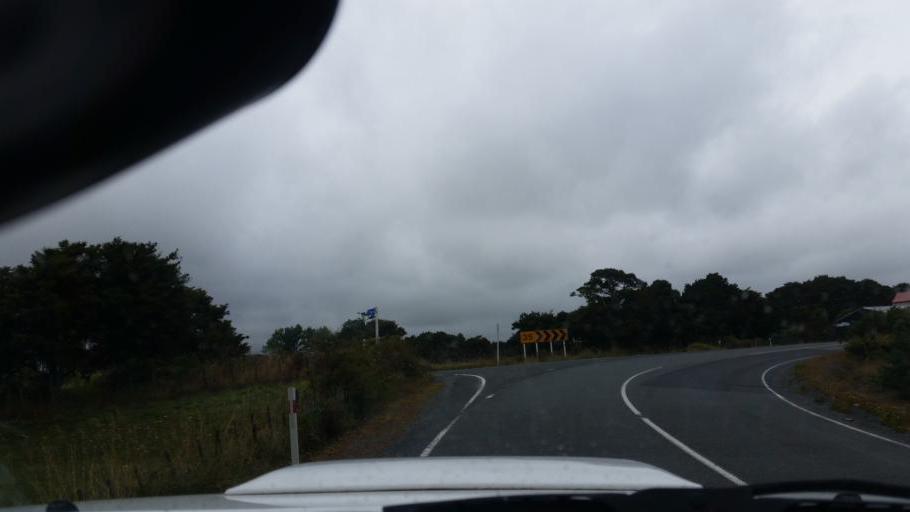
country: NZ
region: Auckland
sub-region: Auckland
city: Wellsford
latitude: -36.1388
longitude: 174.5073
